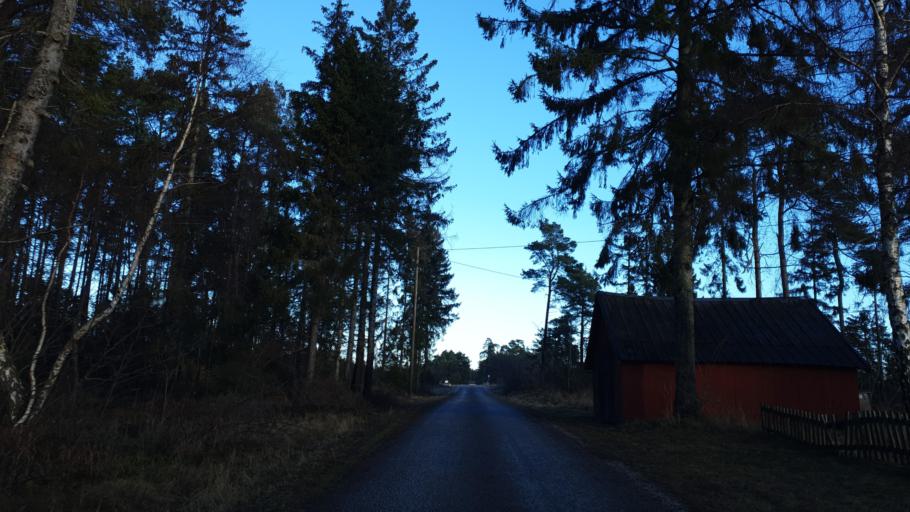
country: SE
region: Gotland
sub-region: Gotland
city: Slite
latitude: 57.3783
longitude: 18.8037
